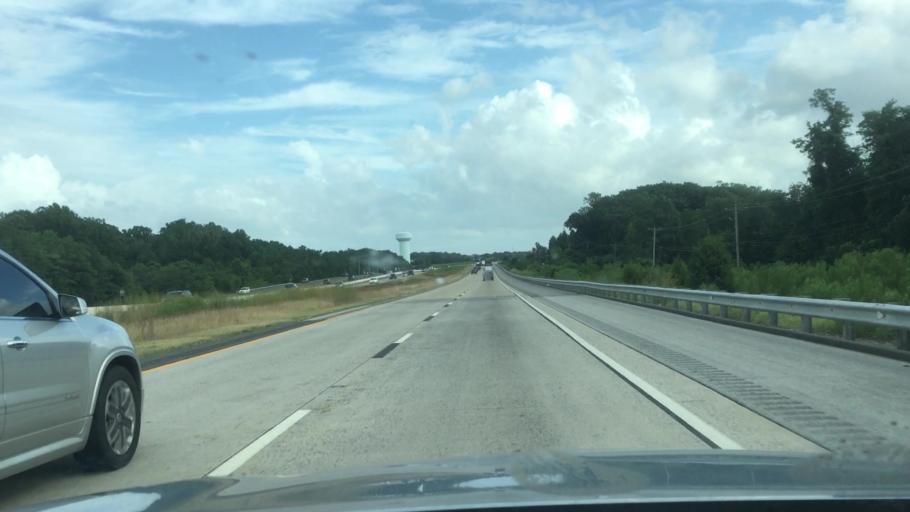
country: US
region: Delaware
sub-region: New Castle County
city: Townsend
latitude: 39.4344
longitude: -75.6607
